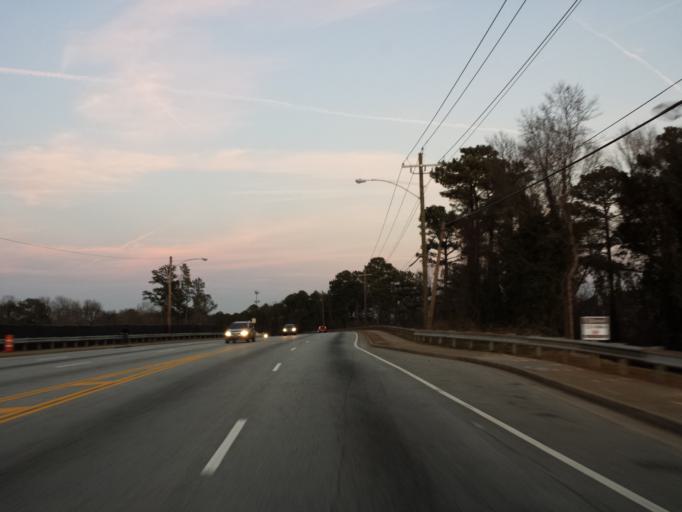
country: US
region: Georgia
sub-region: Cobb County
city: Smyrna
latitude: 33.8802
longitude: -84.5113
